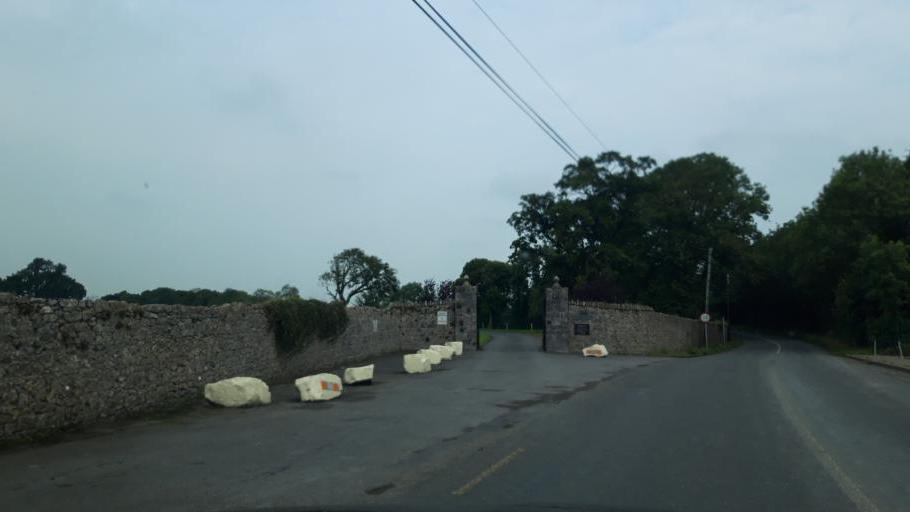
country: IE
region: Leinster
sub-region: Kilkenny
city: Callan
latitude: 52.5148
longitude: -7.5080
